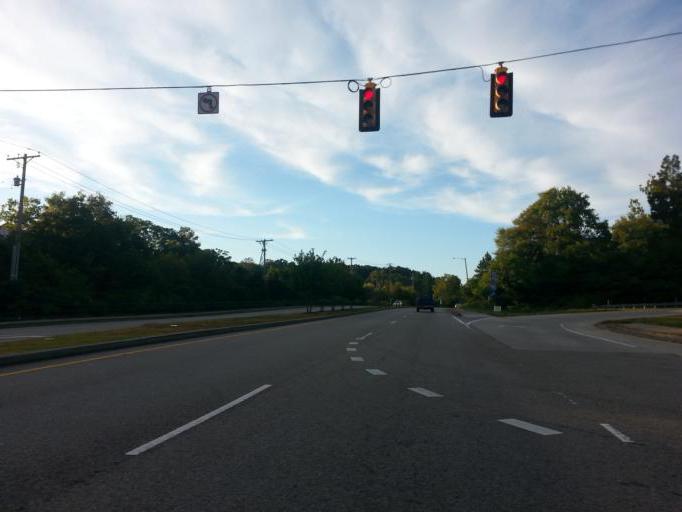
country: US
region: Tennessee
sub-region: Knox County
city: Knoxville
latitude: 35.9389
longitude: -84.0096
